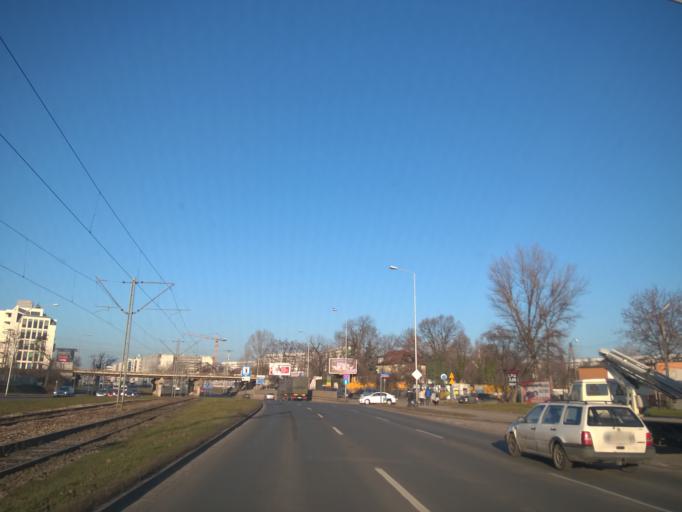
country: PL
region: Lower Silesian Voivodeship
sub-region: Powiat wroclawski
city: Wroclaw
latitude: 51.1192
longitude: 16.9978
